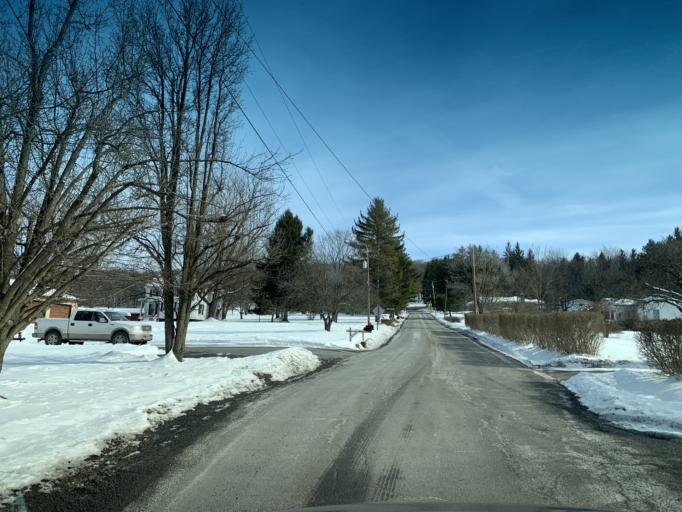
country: US
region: Maryland
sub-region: Allegany County
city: Frostburg
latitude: 39.6727
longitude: -78.8934
